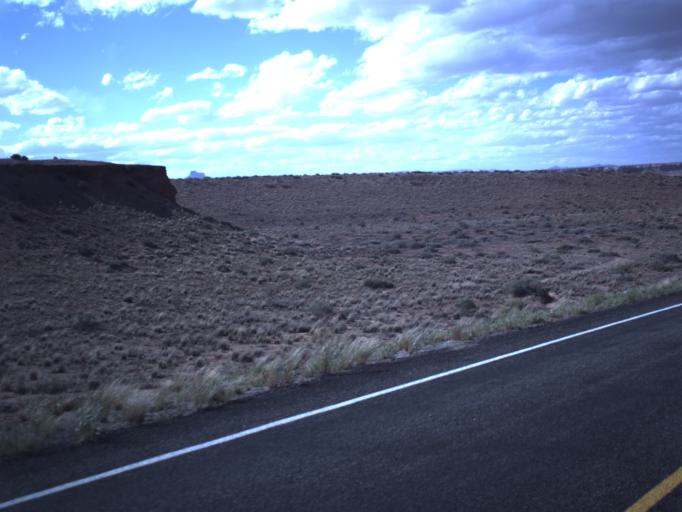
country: US
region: Utah
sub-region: Emery County
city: Ferron
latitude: 38.3551
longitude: -110.6967
